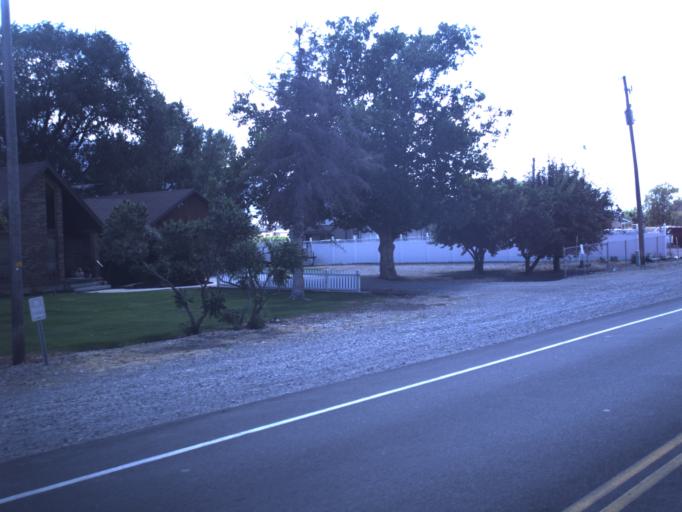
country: US
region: Utah
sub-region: Box Elder County
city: Elwood
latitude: 41.6959
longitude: -112.1418
